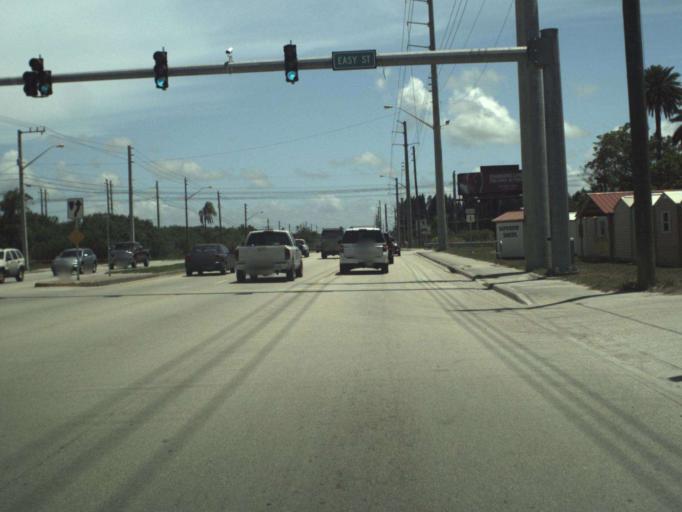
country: US
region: Florida
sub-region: Saint Lucie County
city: Indian River Estates
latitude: 27.3533
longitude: -80.3260
